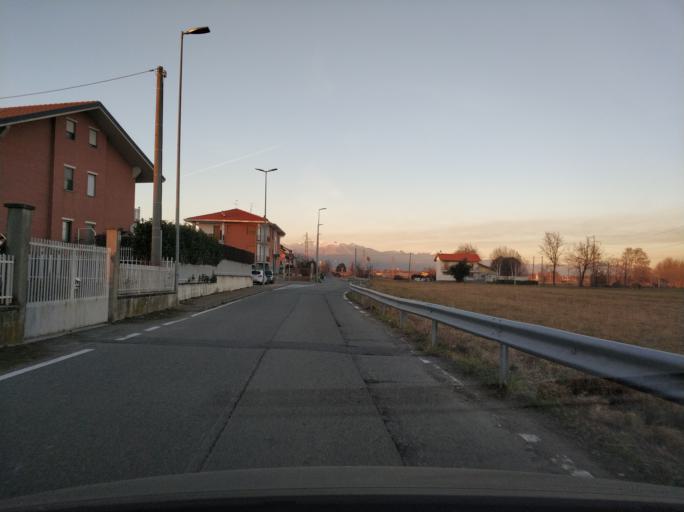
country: IT
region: Piedmont
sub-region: Provincia di Torino
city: San Maurizio
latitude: 45.2108
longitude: 7.6390
